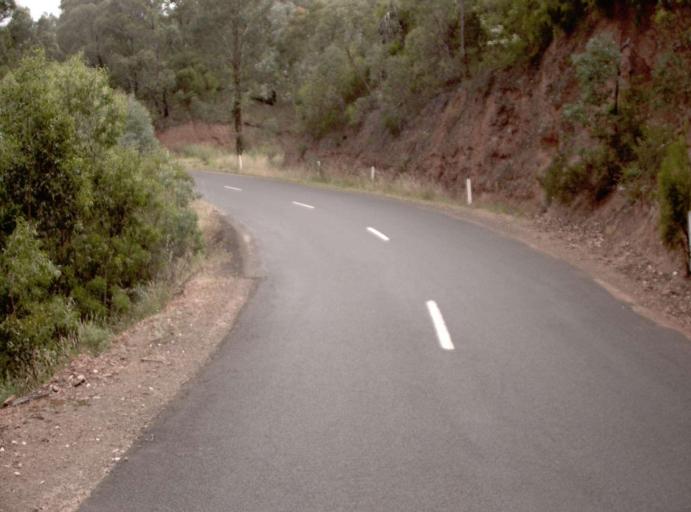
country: AU
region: Victoria
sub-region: Wellington
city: Heyfield
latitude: -37.7540
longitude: 146.6689
